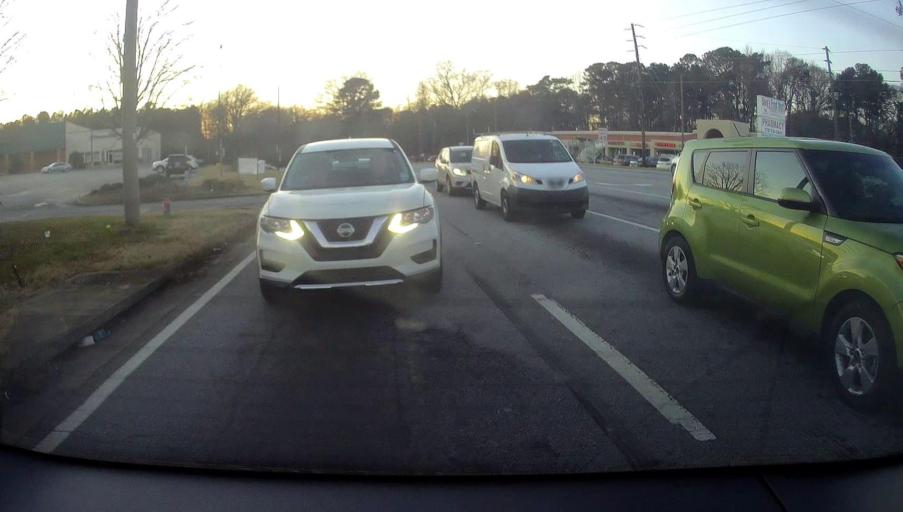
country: US
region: Georgia
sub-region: Clayton County
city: Riverdale
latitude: 33.5500
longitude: -84.4155
